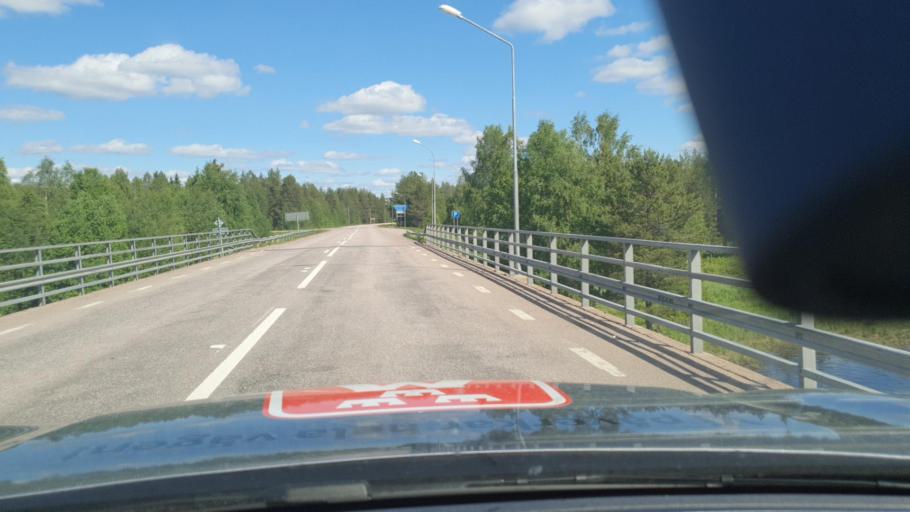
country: SE
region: Norrbotten
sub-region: Pajala Kommun
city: Pajala
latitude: 67.1599
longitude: 22.6321
